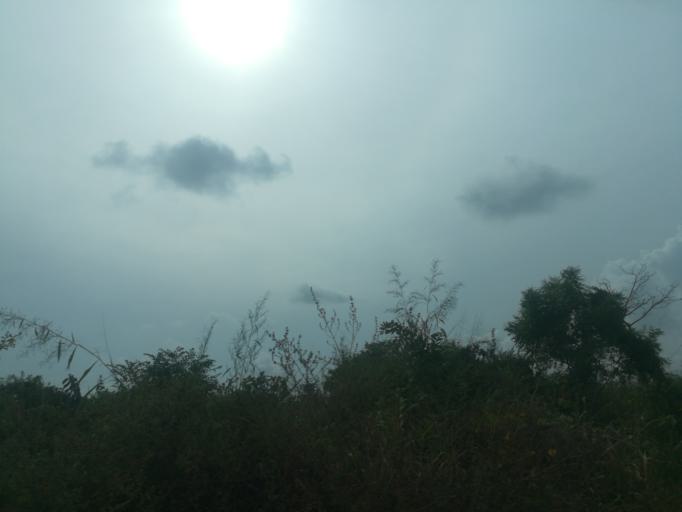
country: NG
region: Ogun
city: Ayetoro
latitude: 7.3152
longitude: 3.0704
